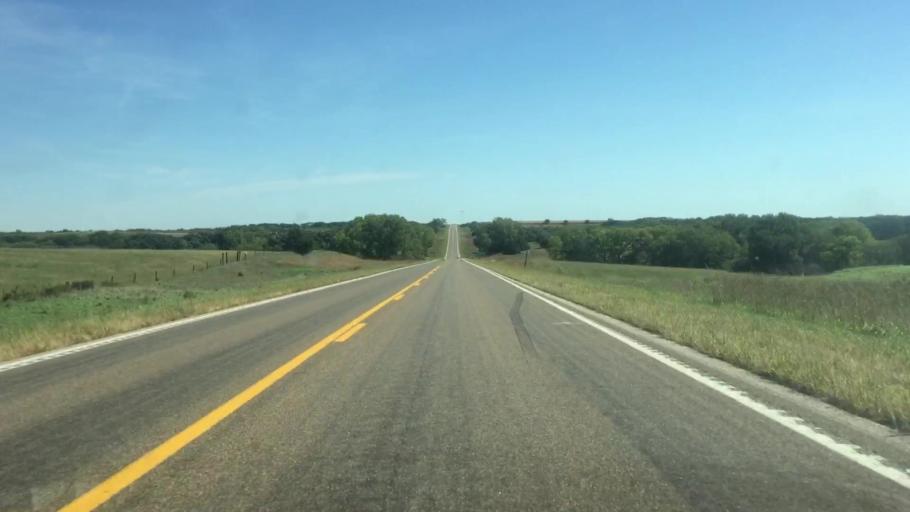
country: US
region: Nebraska
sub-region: Thayer County
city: Hebron
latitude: 40.1472
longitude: -97.5040
